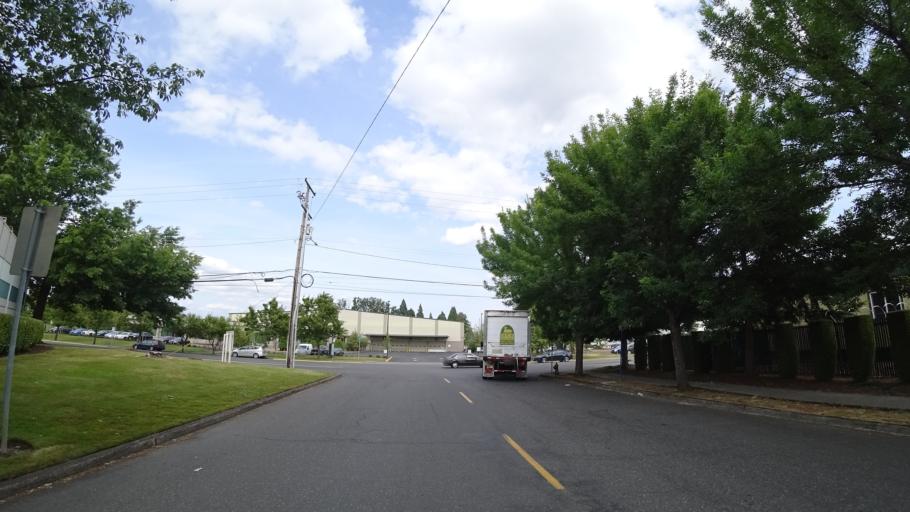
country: US
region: Washington
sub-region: Clark County
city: Vancouver
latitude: 45.5802
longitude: -122.6338
